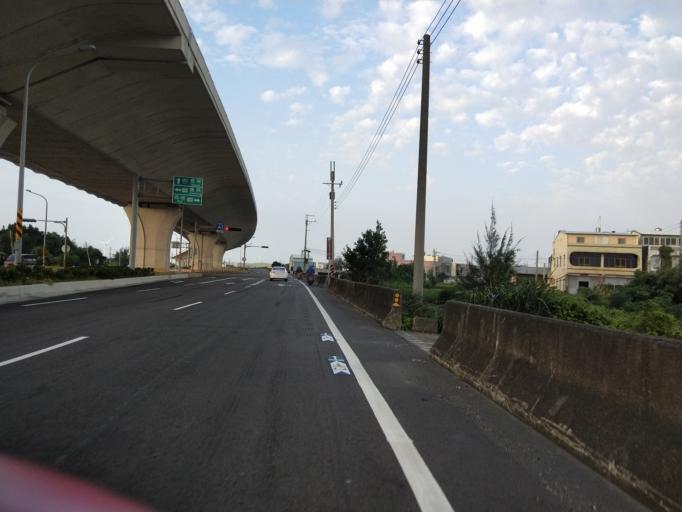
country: TW
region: Taiwan
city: Fengyuan
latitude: 24.4146
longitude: 120.6175
